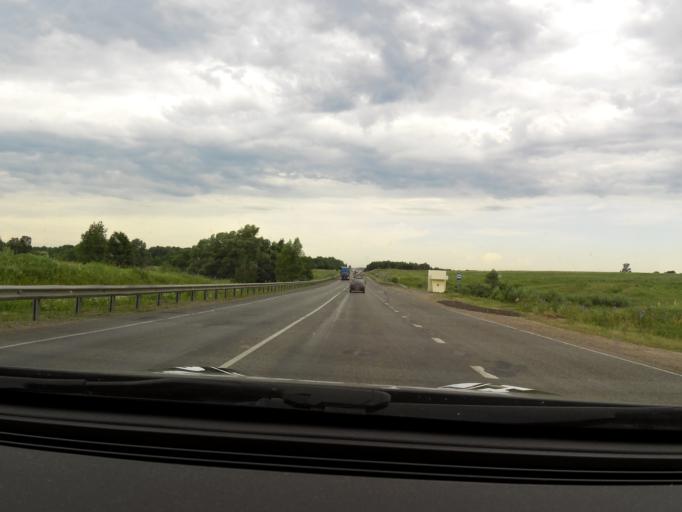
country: RU
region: Bashkortostan
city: Kudeyevskiy
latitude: 54.8172
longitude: 56.7911
